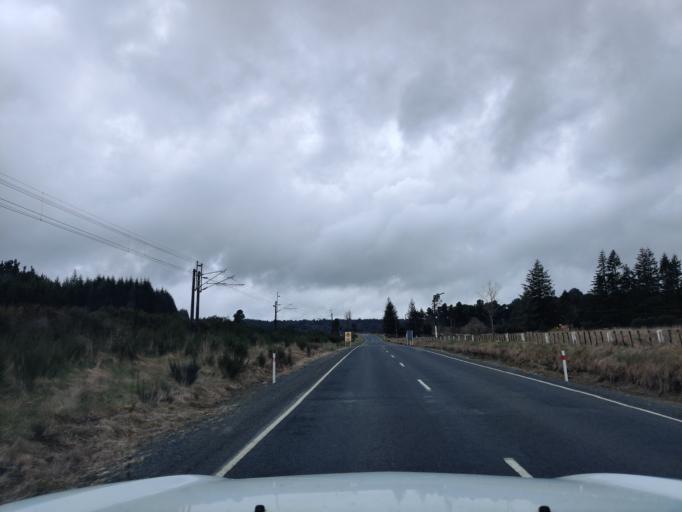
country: NZ
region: Manawatu-Wanganui
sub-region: Ruapehu District
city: Waiouru
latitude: -39.2134
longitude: 175.4010
